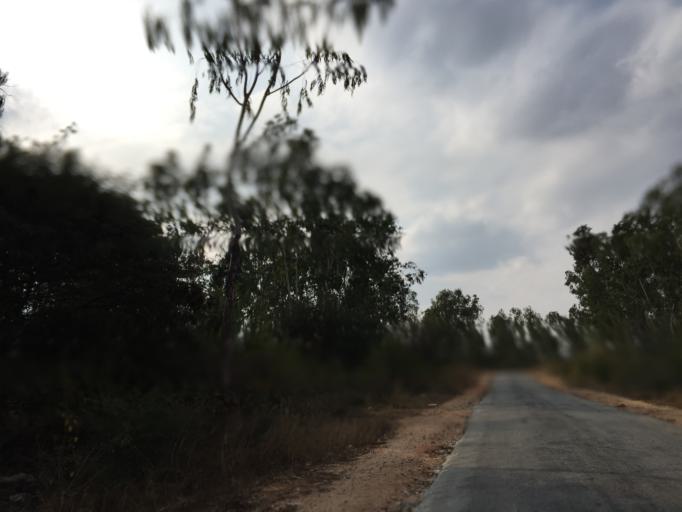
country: IN
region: Karnataka
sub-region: Chikkaballapur
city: Chik Ballapur
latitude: 13.5484
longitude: 77.7732
